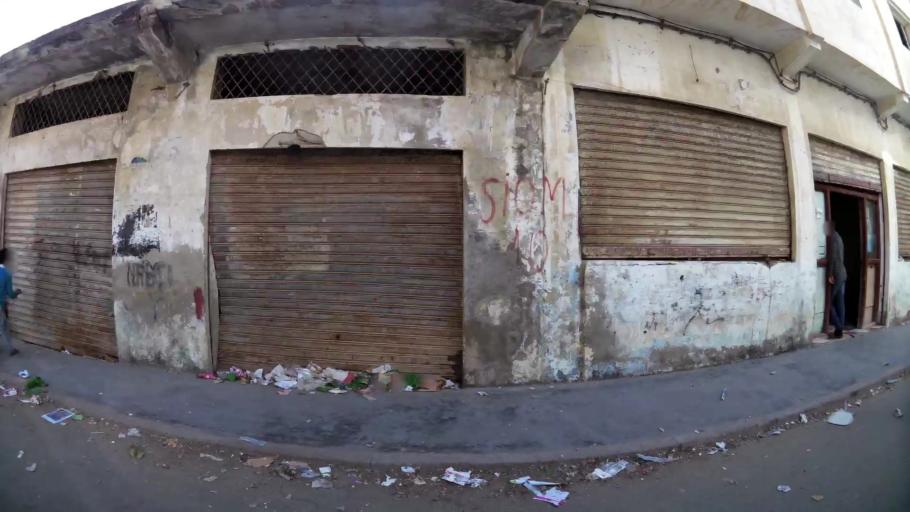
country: MA
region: Tanger-Tetouan
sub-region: Tetouan
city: Martil
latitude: 35.6122
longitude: -5.2731
